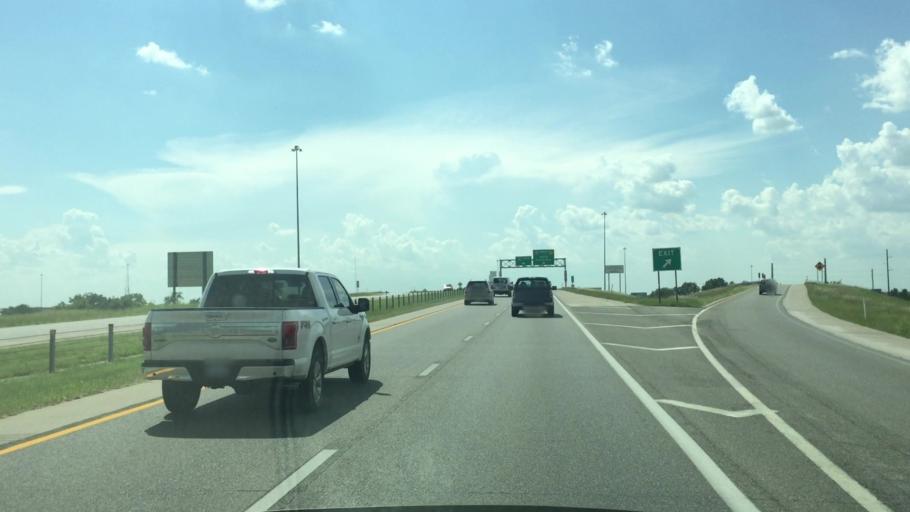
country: US
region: Kansas
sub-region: Sedgwick County
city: Bellaire
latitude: 37.7424
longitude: -97.3130
